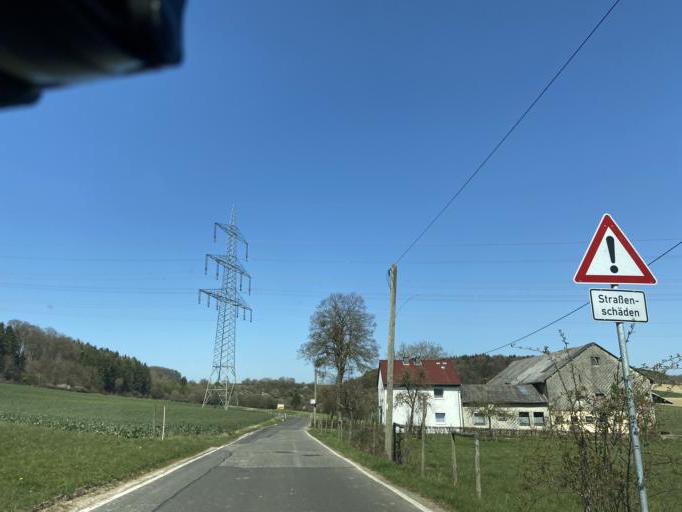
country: DE
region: Rheinland-Pfalz
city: Newel
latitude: 49.7977
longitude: 6.5832
